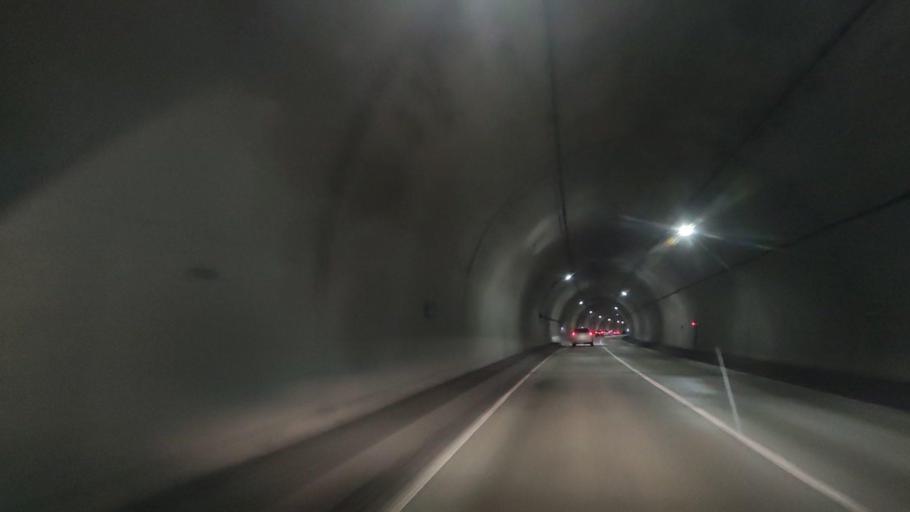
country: JP
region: Hokkaido
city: Ishikari
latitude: 43.5221
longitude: 141.3928
